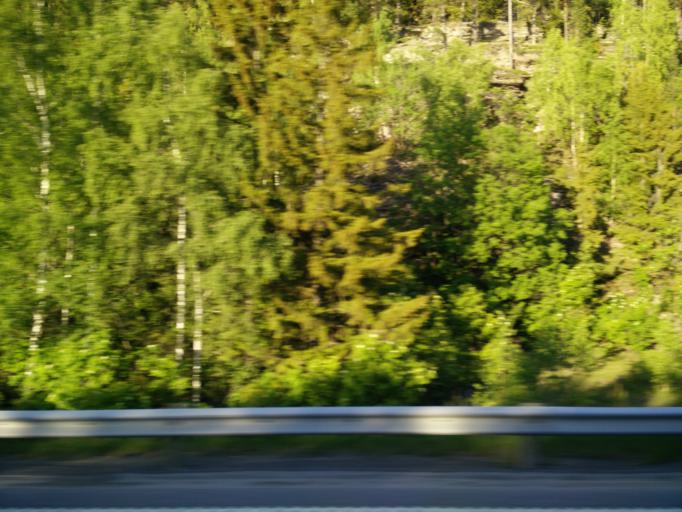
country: NO
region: Buskerud
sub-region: Hole
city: Vik
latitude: 60.0188
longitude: 10.2683
